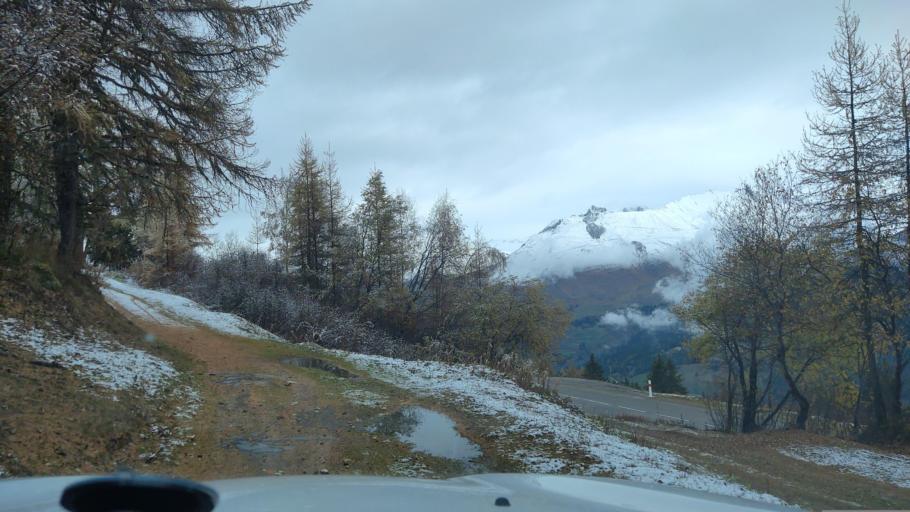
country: FR
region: Rhone-Alpes
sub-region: Departement de la Savoie
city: Seez
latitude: 45.5953
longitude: 6.8243
